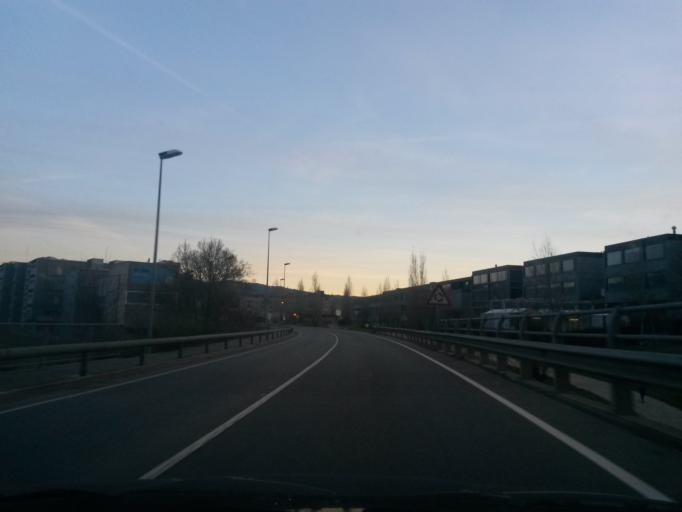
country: ES
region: Catalonia
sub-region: Provincia de Girona
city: Girona
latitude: 41.9687
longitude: 2.8361
